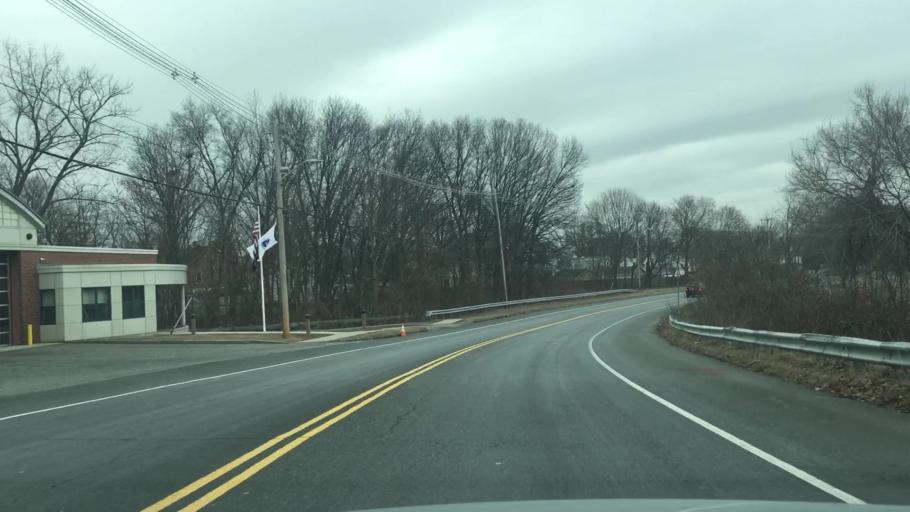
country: US
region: Massachusetts
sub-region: Hampden County
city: Holyoke
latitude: 42.1878
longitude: -72.6337
